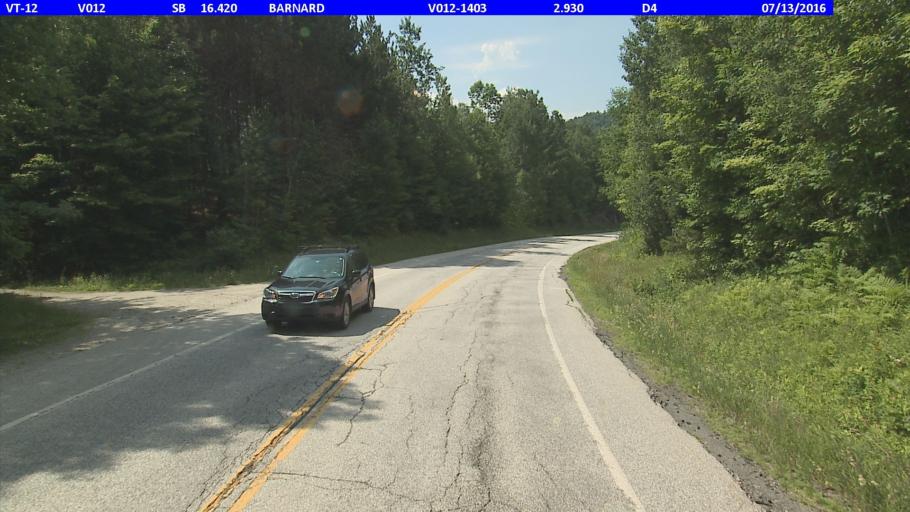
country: US
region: Vermont
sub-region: Windsor County
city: Woodstock
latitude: 43.7040
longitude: -72.6185
